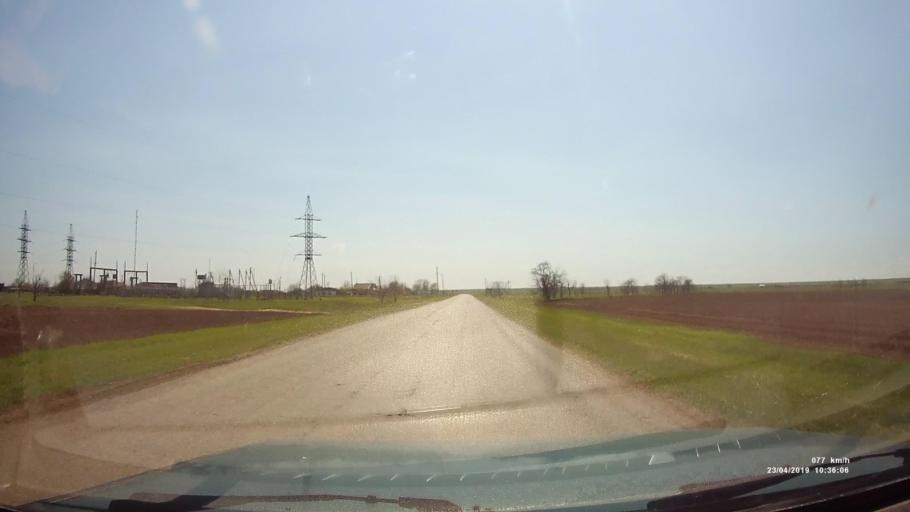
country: RU
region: Kalmykiya
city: Yashalta
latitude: 46.5481
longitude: 42.6320
